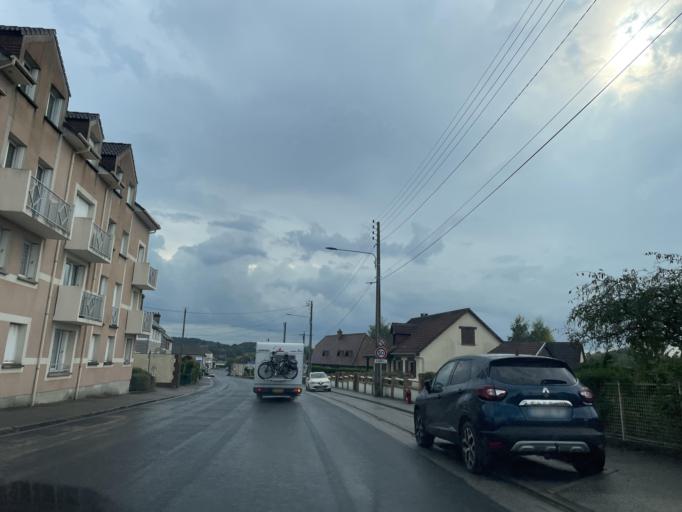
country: FR
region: Haute-Normandie
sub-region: Departement de la Seine-Maritime
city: Neufchatel-en-Bray
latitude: 49.7353
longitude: 1.4369
